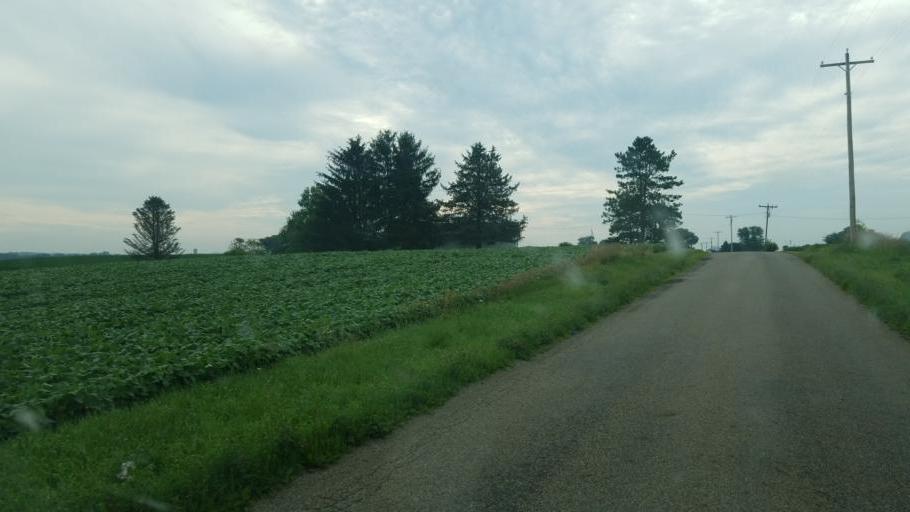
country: US
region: Ohio
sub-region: Knox County
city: Fredericktown
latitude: 40.4520
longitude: -82.5844
